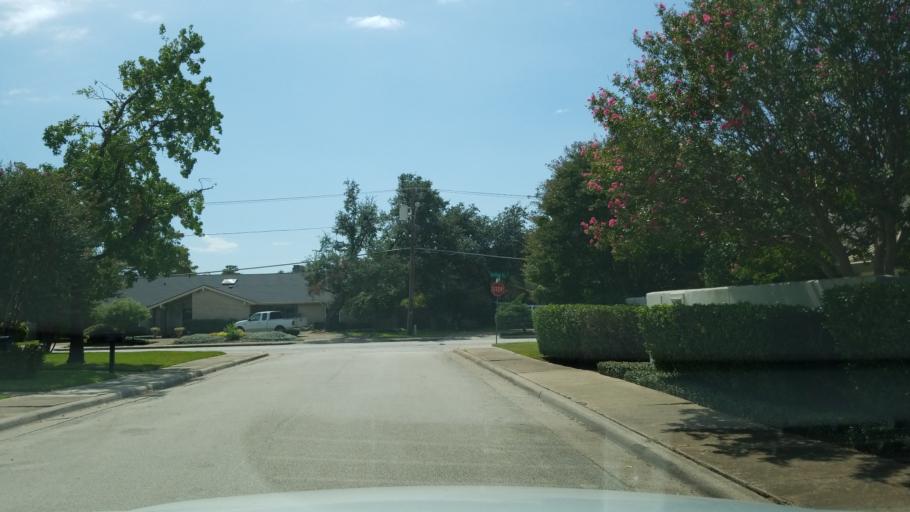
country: US
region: Texas
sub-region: Dallas County
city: Addison
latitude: 32.9600
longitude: -96.7853
